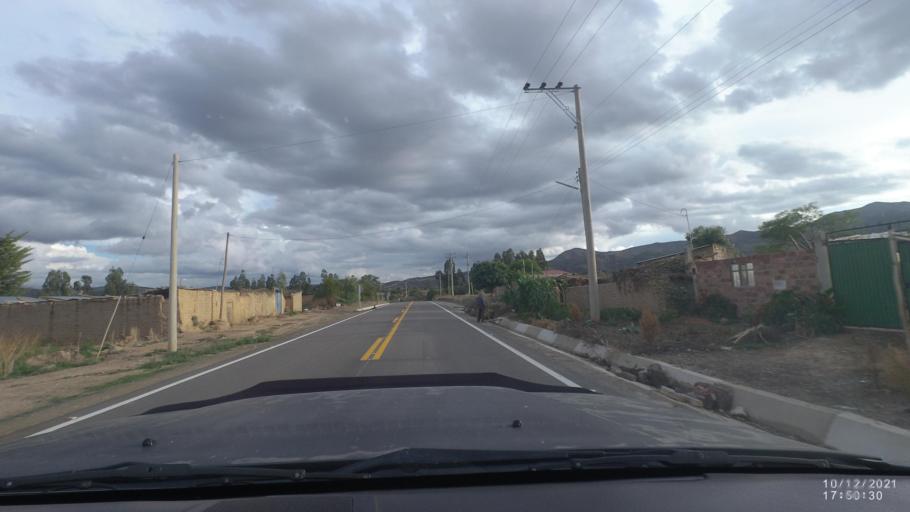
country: BO
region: Cochabamba
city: Tarata
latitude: -17.6669
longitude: -65.9635
